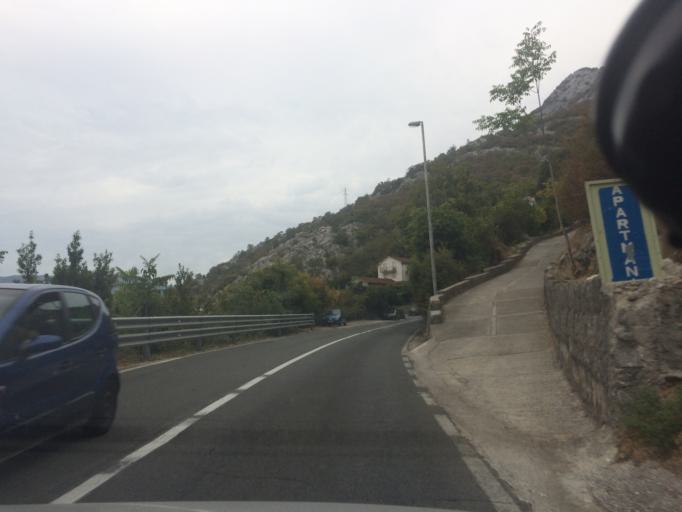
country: ME
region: Kotor
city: Risan
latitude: 42.5159
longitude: 18.6841
